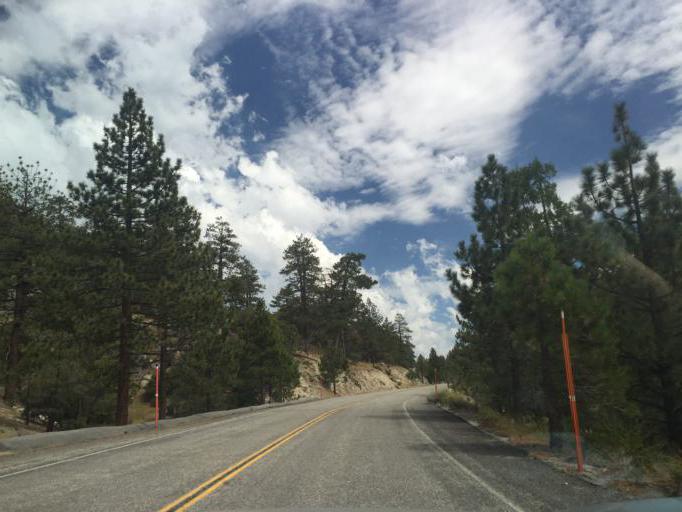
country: US
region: California
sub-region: Los Angeles County
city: Littlerock
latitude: 34.3530
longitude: -117.9436
